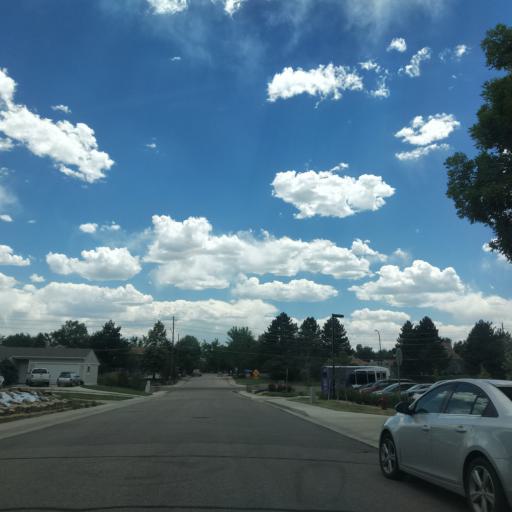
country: US
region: Colorado
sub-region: Jefferson County
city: Lakewood
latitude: 39.6832
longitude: -105.0885
